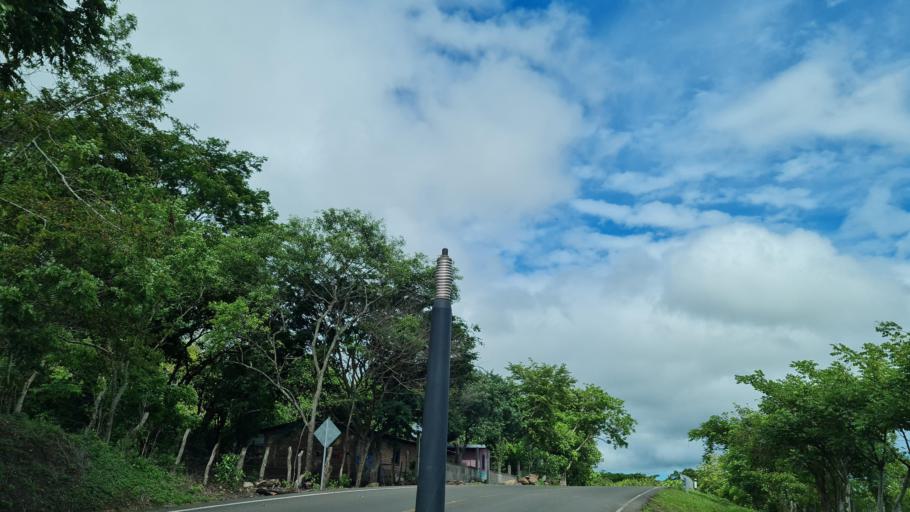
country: NI
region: Boaco
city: San Jose de los Remates
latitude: 12.6114
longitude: -85.8925
